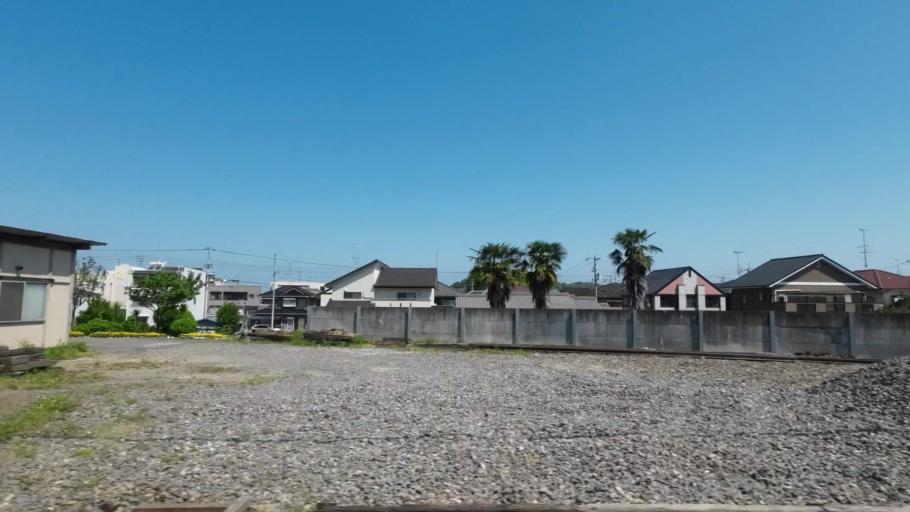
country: JP
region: Ehime
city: Niihama
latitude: 33.9706
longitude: 133.3250
